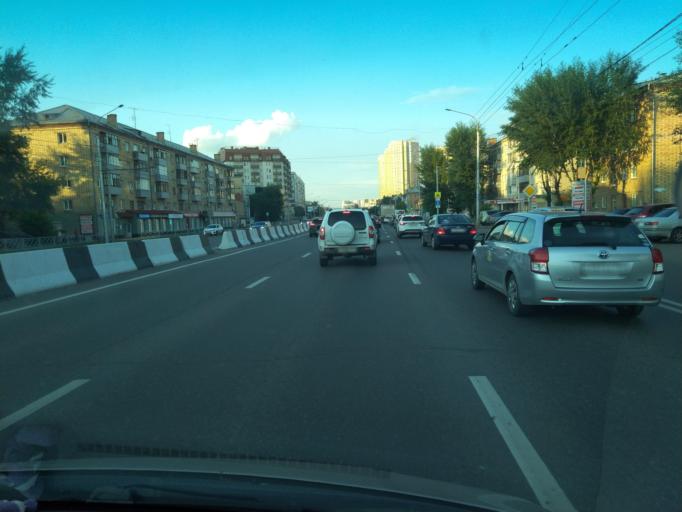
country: RU
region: Krasnoyarskiy
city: Krasnoyarsk
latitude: 56.0294
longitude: 92.9149
